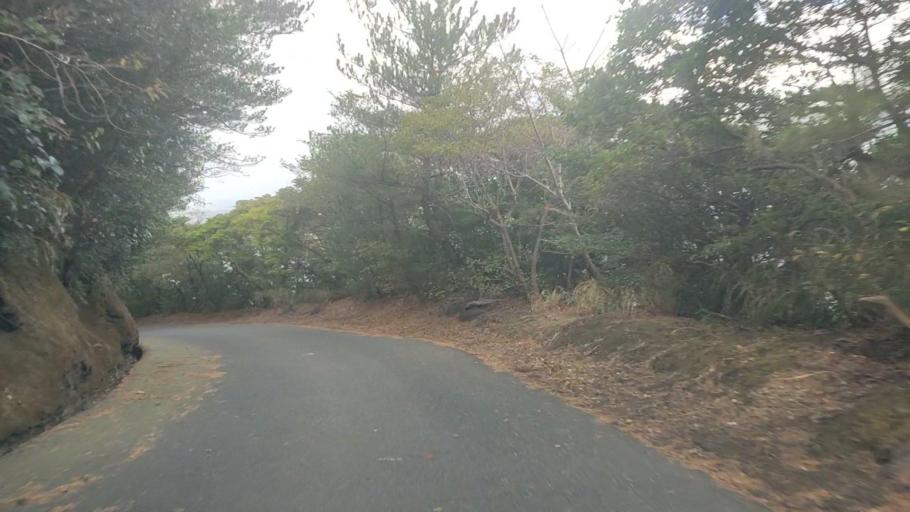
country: JP
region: Kagoshima
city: Kagoshima-shi
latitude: 31.5947
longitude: 130.6342
